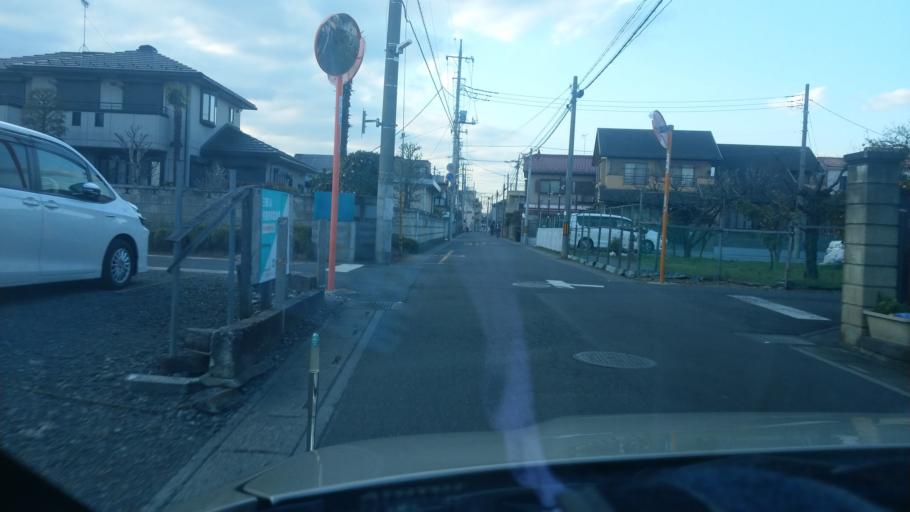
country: JP
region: Saitama
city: Yono
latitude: 35.8917
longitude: 139.6021
